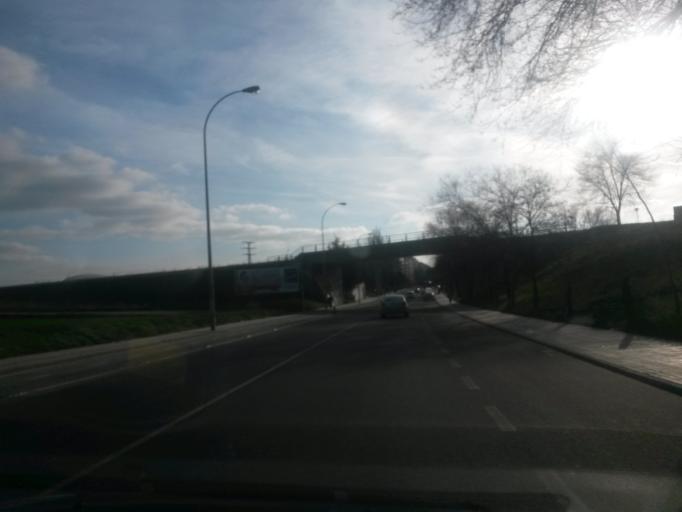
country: ES
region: Castille and Leon
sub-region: Provincia de Salamanca
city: Salamanca
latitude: 40.9824
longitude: -5.6500
